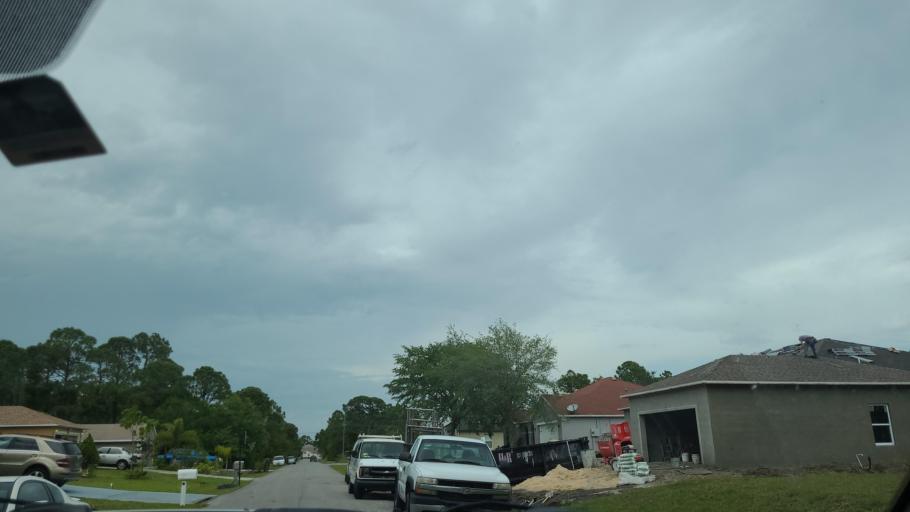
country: US
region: Florida
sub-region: Brevard County
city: Grant-Valkaria
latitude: 27.9405
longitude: -80.6266
